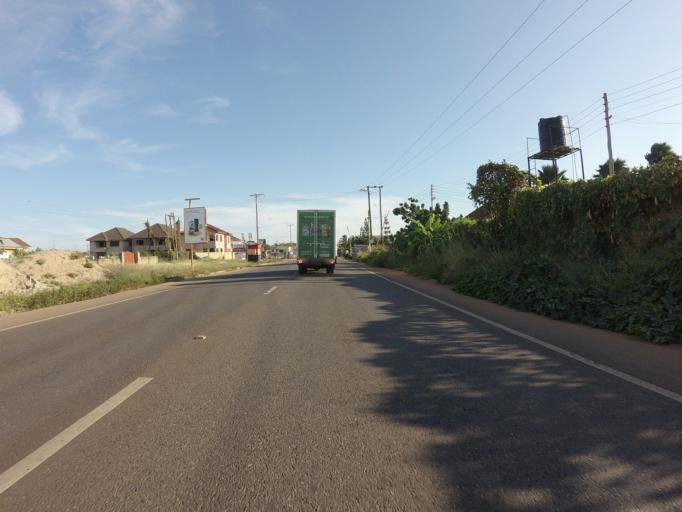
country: GH
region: Greater Accra
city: Nungua
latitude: 5.6425
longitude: -0.0926
